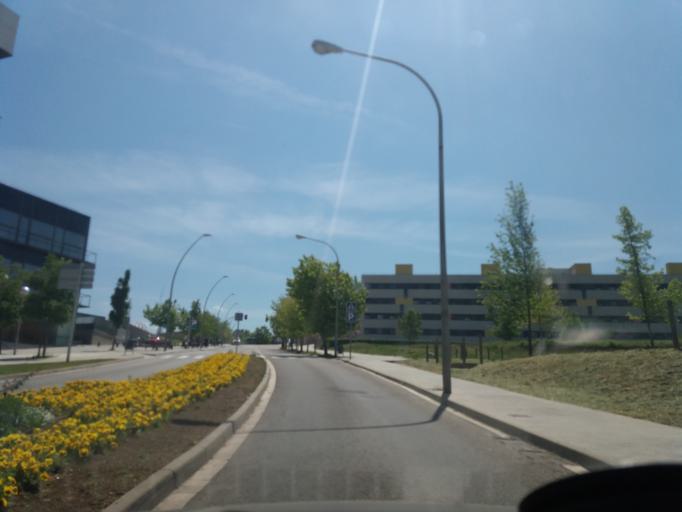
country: ES
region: Catalonia
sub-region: Provincia de Barcelona
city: Manresa
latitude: 41.7203
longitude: 1.8366
